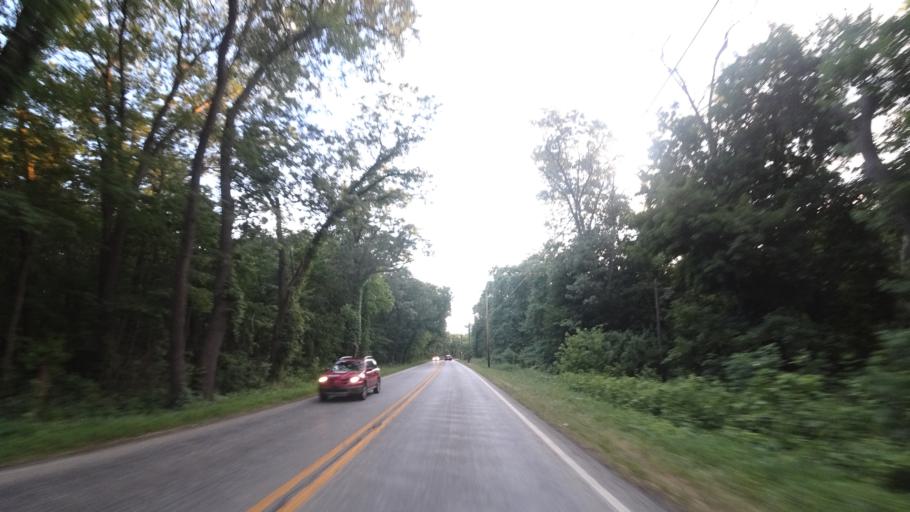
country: US
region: Indiana
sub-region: Porter County
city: Porter
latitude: 41.6368
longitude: -87.0809
